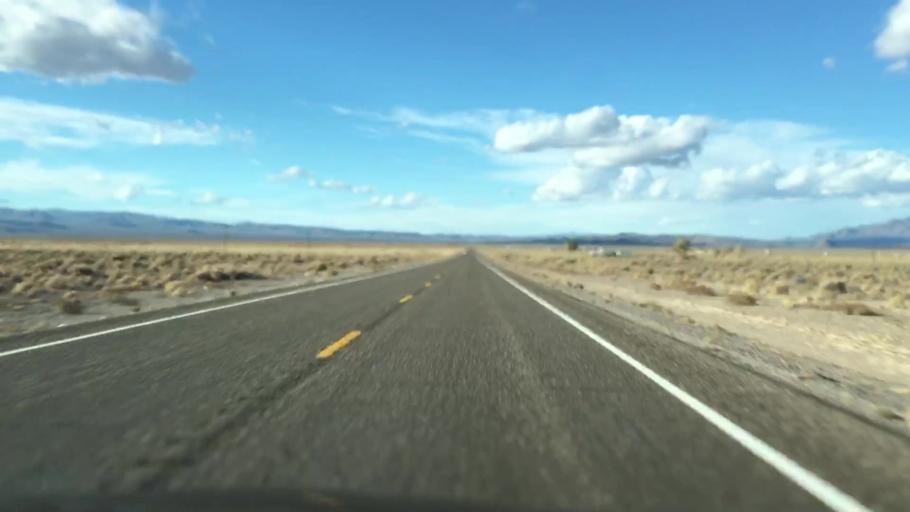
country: US
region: Nevada
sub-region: Nye County
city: Beatty
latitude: 37.2471
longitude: -117.0008
